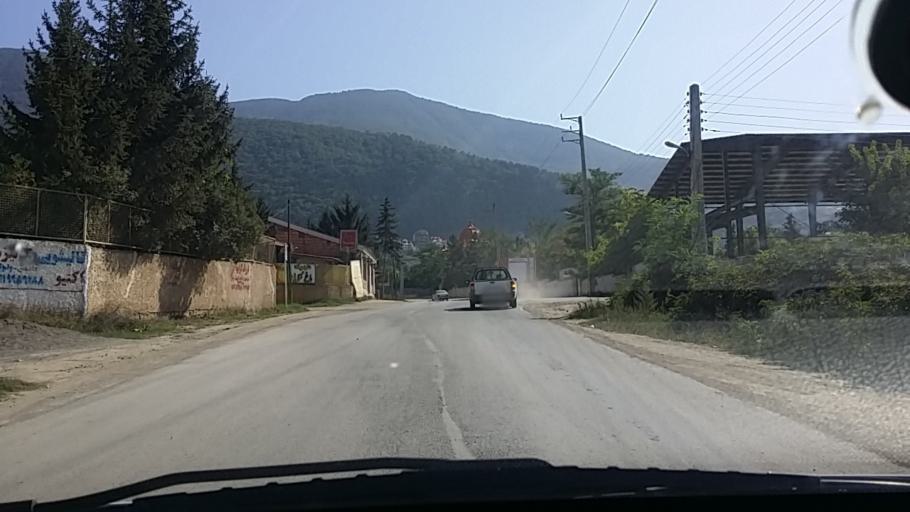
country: IR
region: Mazandaran
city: `Abbasabad
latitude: 36.5005
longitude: 51.1637
